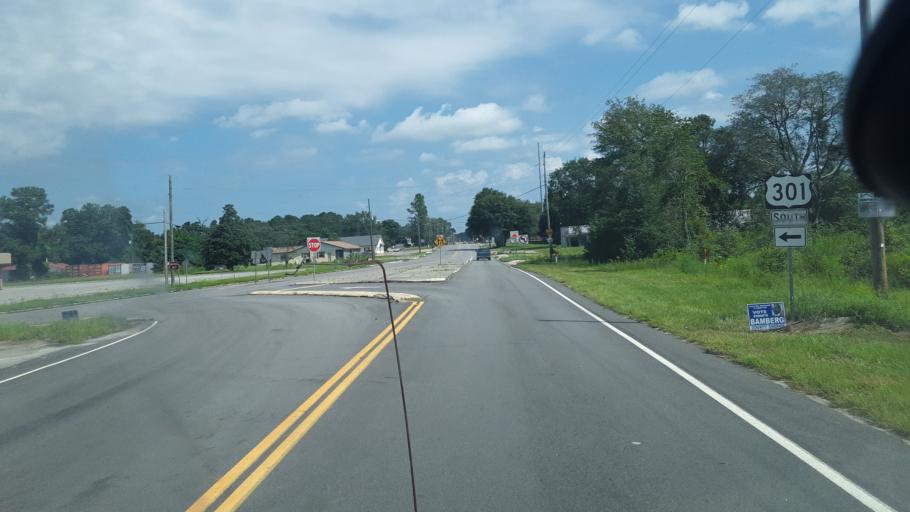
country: US
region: South Carolina
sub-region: Bamberg County
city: Bamberg
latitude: 33.2841
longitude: -81.0398
